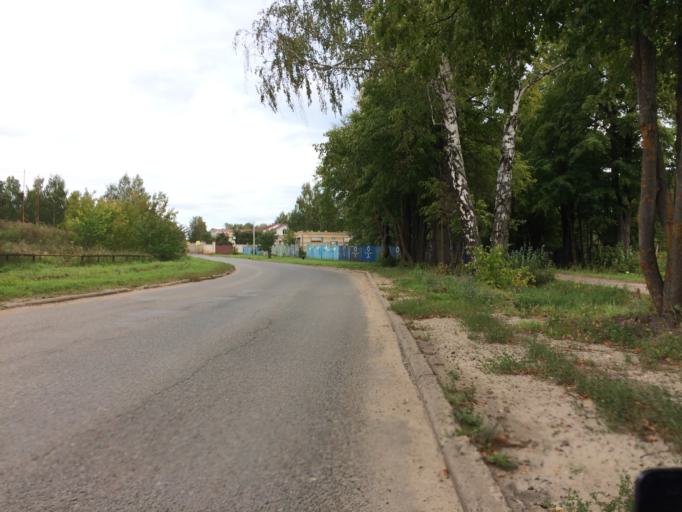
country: RU
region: Mariy-El
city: Yoshkar-Ola
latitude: 56.6494
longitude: 47.9626
